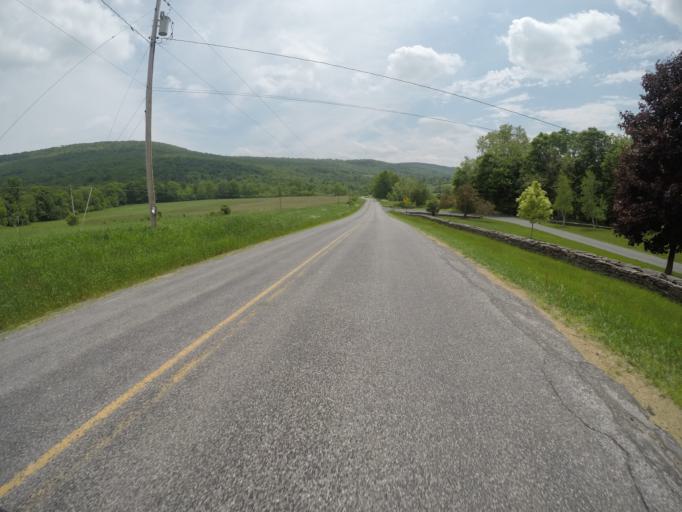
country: US
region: New York
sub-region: Delaware County
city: Stamford
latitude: 42.1964
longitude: -74.6763
